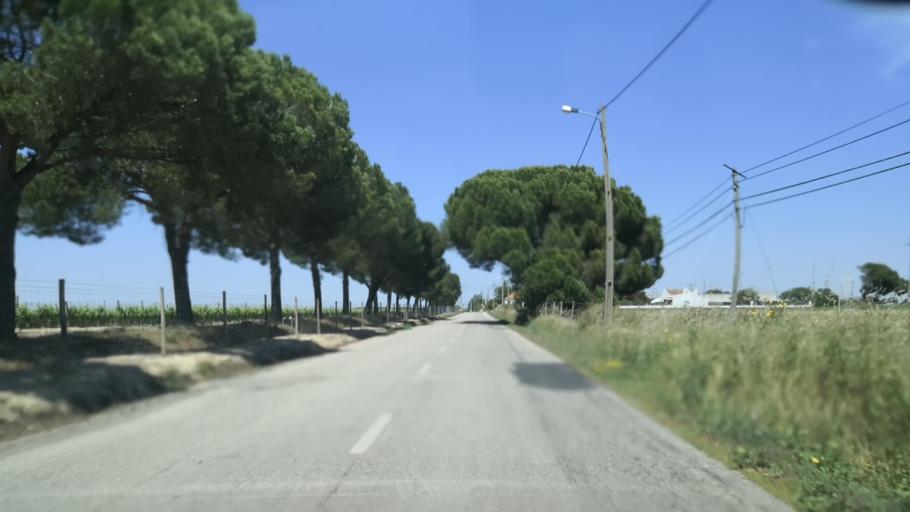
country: PT
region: Santarem
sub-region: Benavente
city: Poceirao
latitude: 38.6782
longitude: -8.7334
